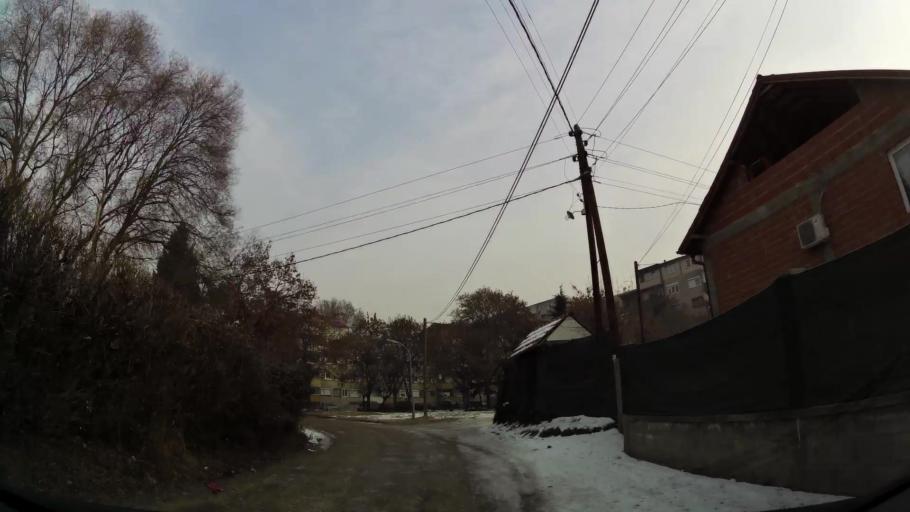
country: MK
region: Cair
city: Cair
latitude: 42.0171
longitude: 21.4416
